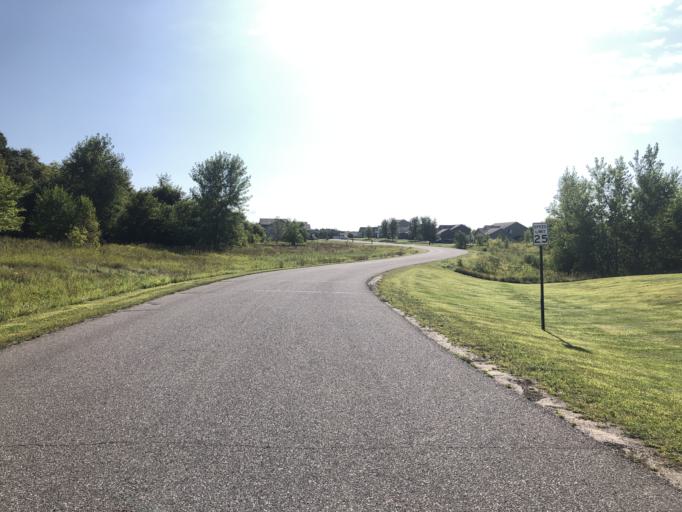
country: US
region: Minnesota
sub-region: Sherburne County
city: Becker
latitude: 45.4257
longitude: -93.8397
